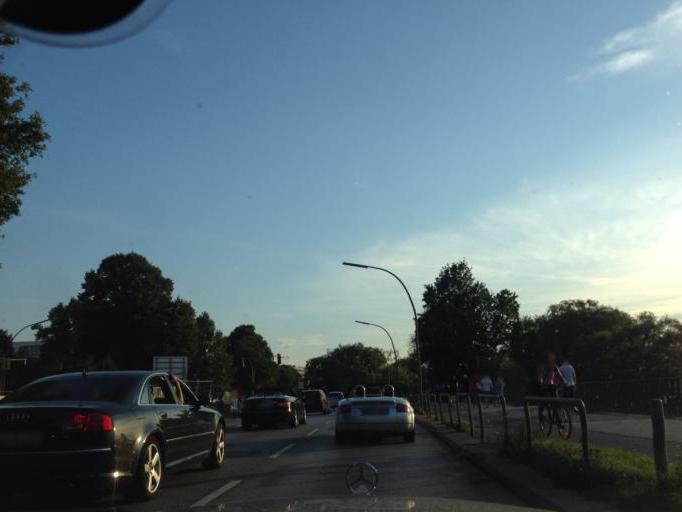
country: DE
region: Hamburg
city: St. Georg
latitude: 53.5634
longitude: 10.0160
